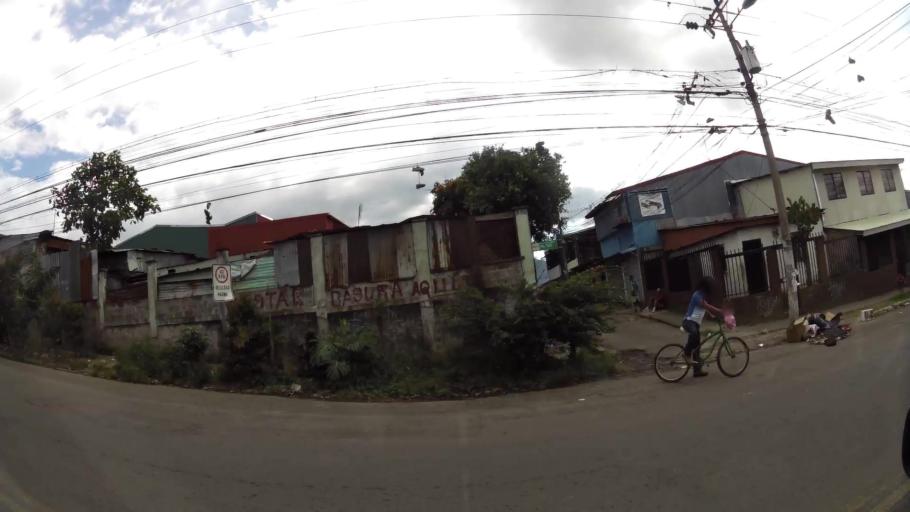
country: CR
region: San Jose
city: San Rafael
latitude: 9.9540
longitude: -84.1511
